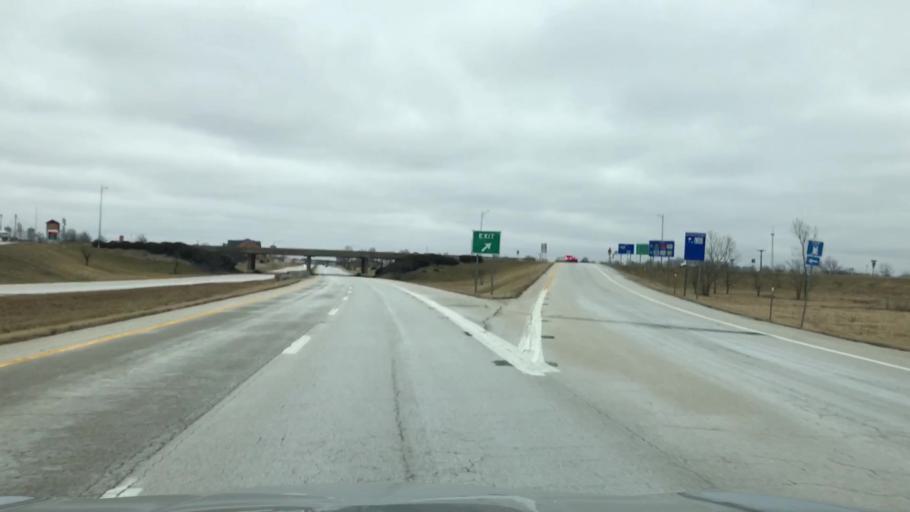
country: US
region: Missouri
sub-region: Livingston County
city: Chillicothe
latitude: 39.7731
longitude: -93.5551
